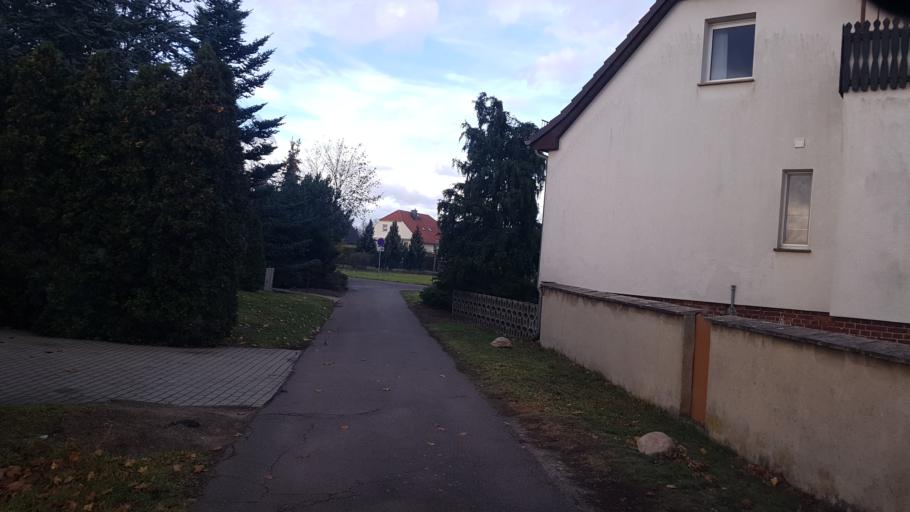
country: DE
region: Brandenburg
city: Falkenberg
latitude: 51.5907
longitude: 13.3008
